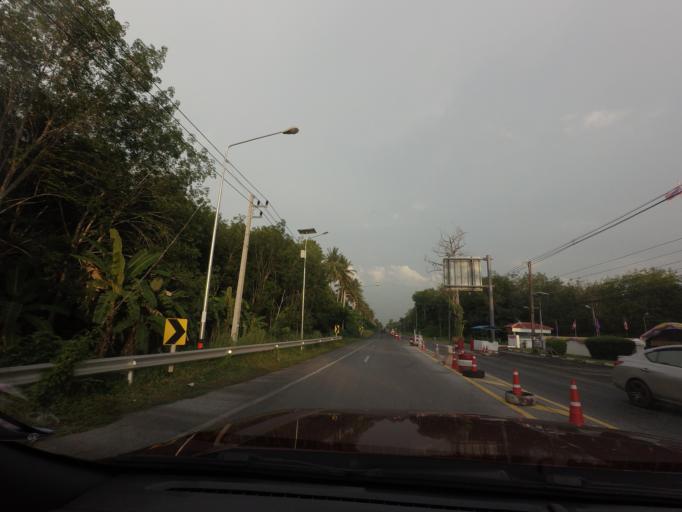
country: TH
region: Pattani
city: Mae Lan
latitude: 6.6628
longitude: 101.1662
